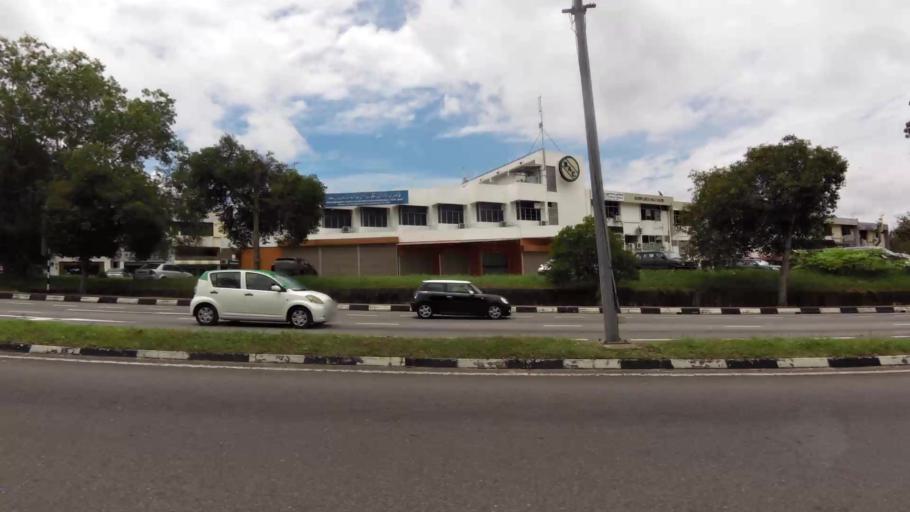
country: BN
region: Brunei and Muara
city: Bandar Seri Begawan
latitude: 4.9097
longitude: 114.9158
